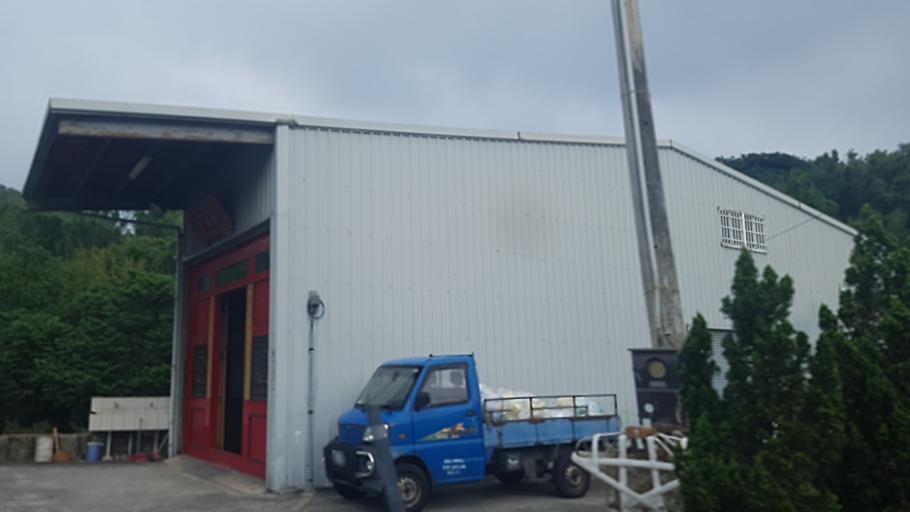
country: TW
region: Taiwan
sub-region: Hsinchu
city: Hsinchu
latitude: 24.7816
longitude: 120.9337
